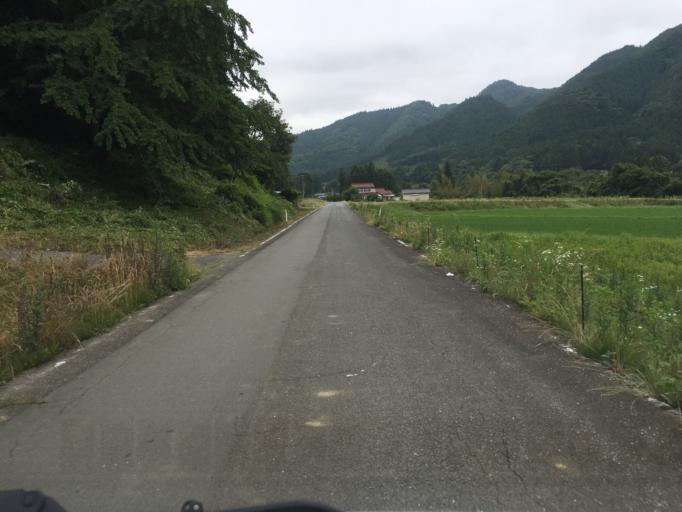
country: JP
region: Miyagi
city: Marumori
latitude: 37.7656
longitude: 140.8450
